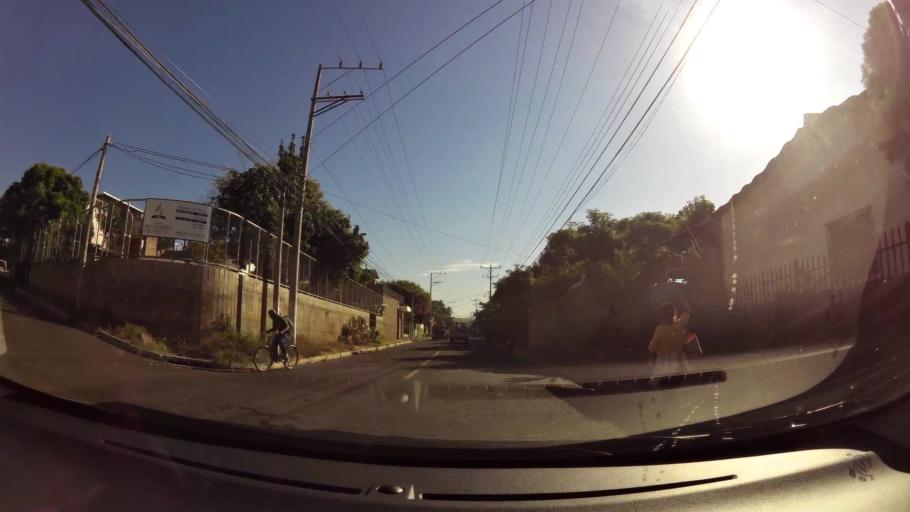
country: SV
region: Sonsonate
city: Sonzacate
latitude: 13.7371
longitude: -89.7141
